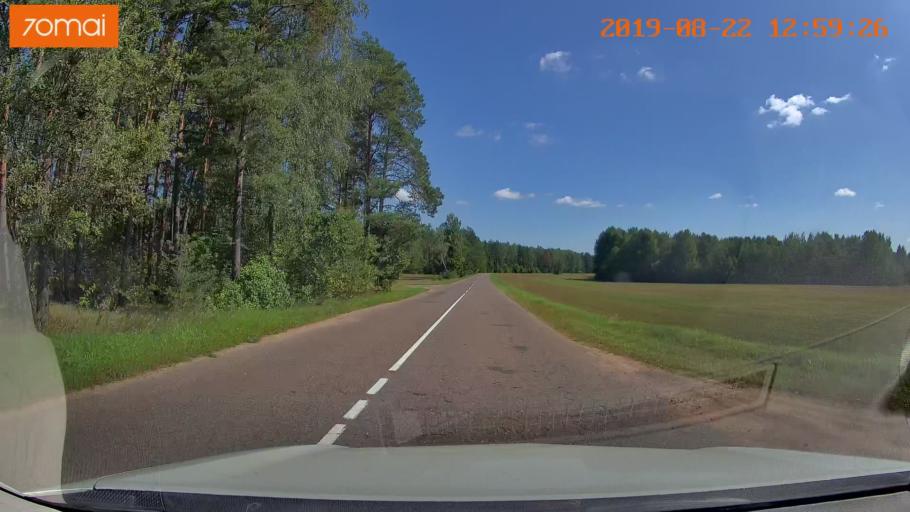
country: BY
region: Minsk
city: Prawdzinski
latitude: 53.4227
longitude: 27.7905
